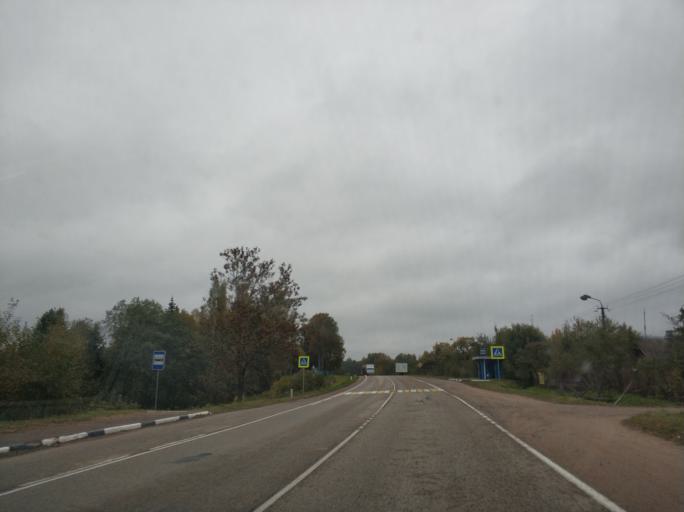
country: BY
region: Vitebsk
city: Rasony
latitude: 56.0560
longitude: 28.7131
